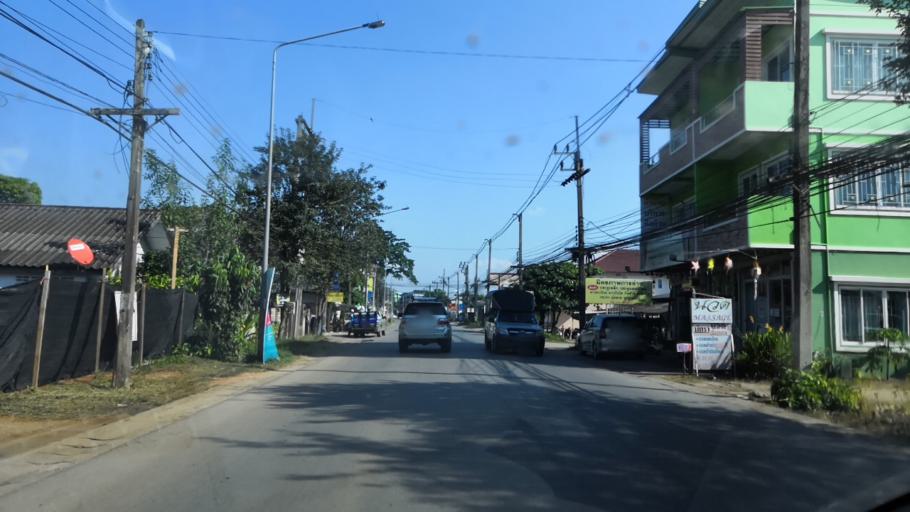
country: TH
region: Chiang Rai
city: Chiang Rai
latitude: 19.9249
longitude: 99.8394
